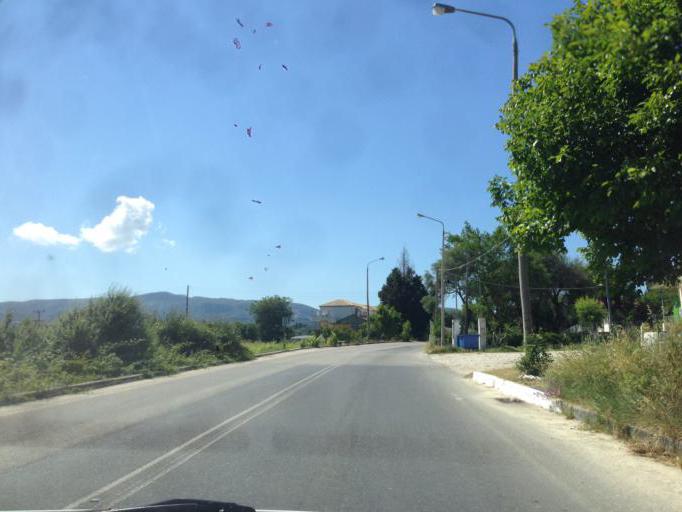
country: GR
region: Ionian Islands
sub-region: Nomos Kerkyras
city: Agios Georgis
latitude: 39.7609
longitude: 19.7196
